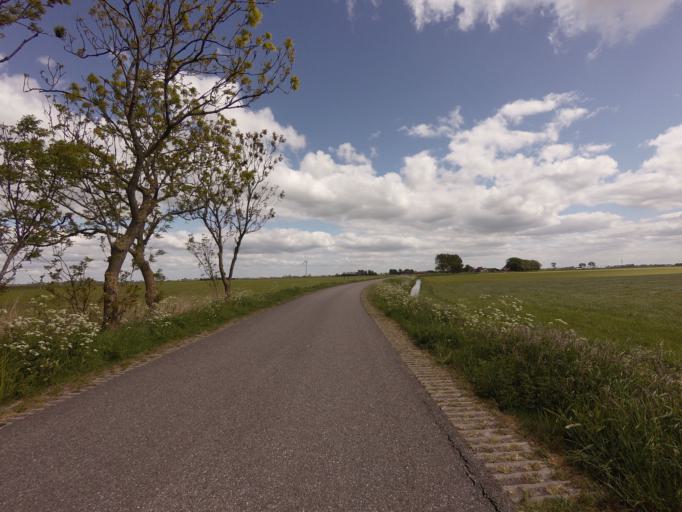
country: NL
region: Friesland
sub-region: Sudwest Fryslan
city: Bolsward
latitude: 53.0832
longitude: 5.5482
